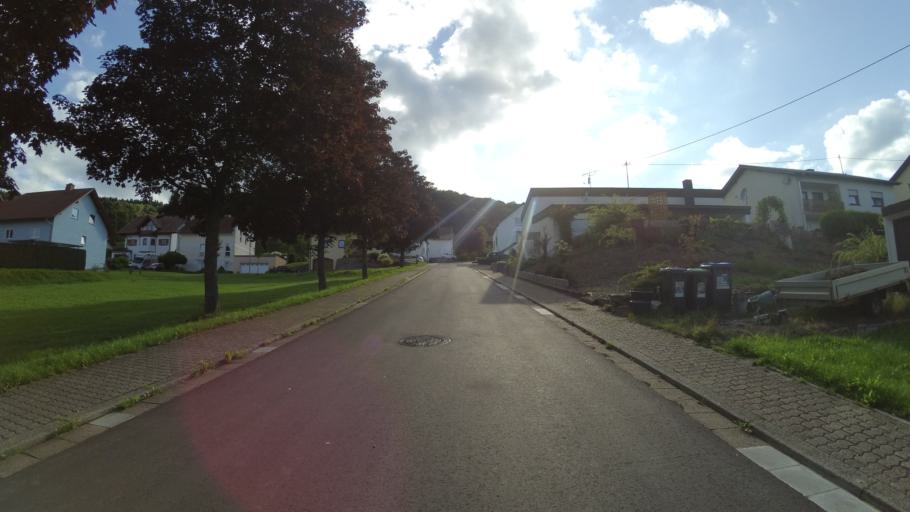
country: DE
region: Saarland
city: Nonnweiler
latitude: 49.5672
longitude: 6.9636
